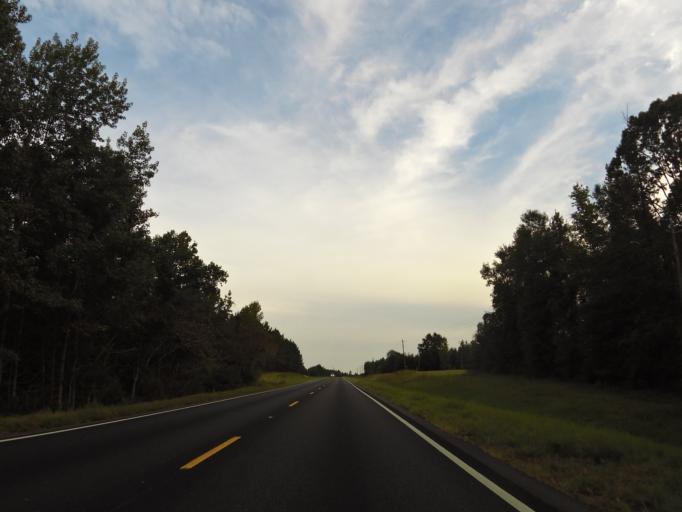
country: US
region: Alabama
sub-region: Monroe County
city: Frisco City
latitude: 31.2384
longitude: -87.4844
